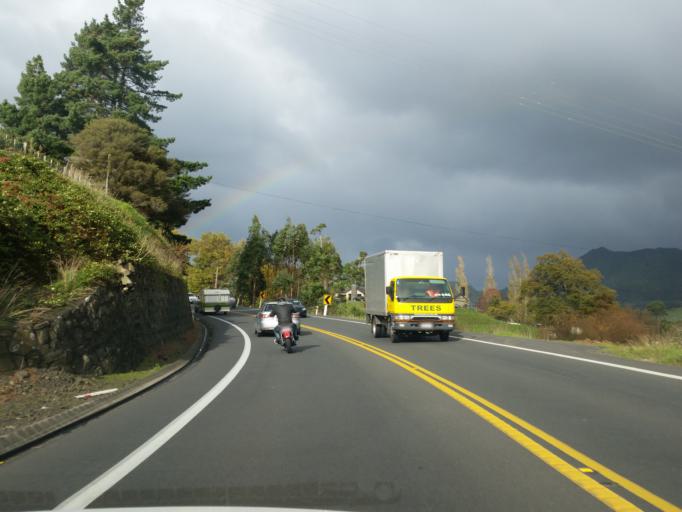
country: NZ
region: Waikato
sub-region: Hauraki District
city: Paeroa
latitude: -37.4025
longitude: 175.6988
